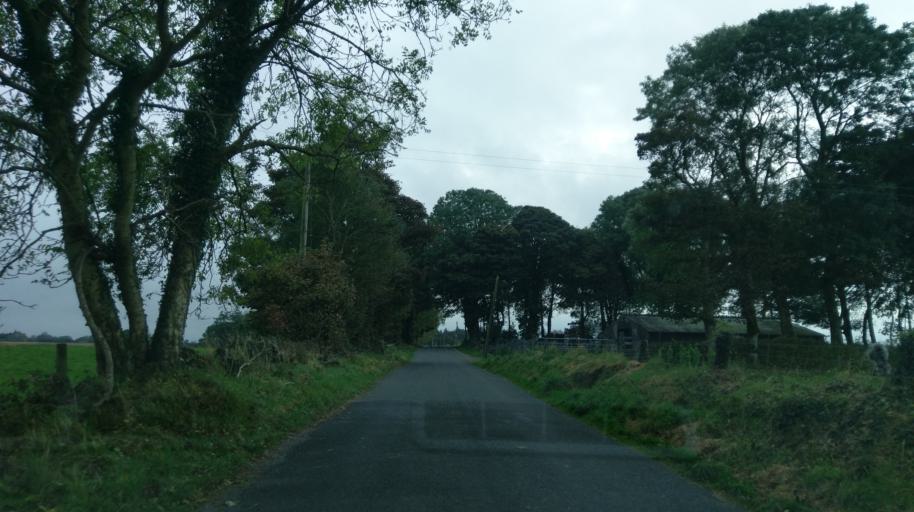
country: IE
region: Connaught
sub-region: County Galway
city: Athenry
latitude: 53.4576
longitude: -8.6112
